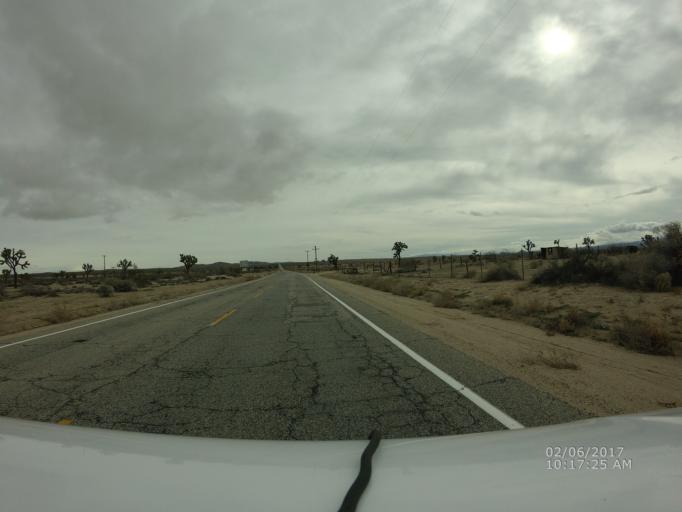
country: US
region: California
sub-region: Los Angeles County
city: Lake Los Angeles
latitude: 34.6899
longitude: -117.7571
